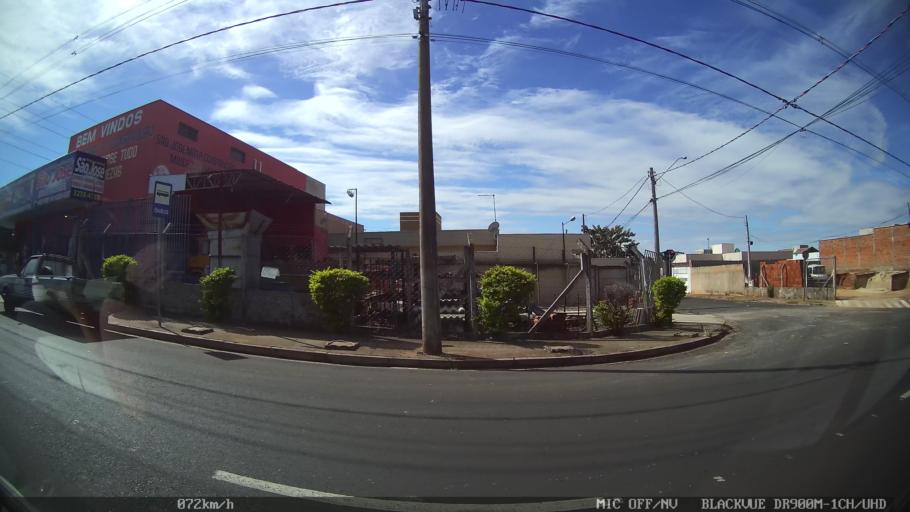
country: BR
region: Sao Paulo
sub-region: Sao Jose Do Rio Preto
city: Sao Jose do Rio Preto
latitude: -20.8336
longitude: -49.3483
